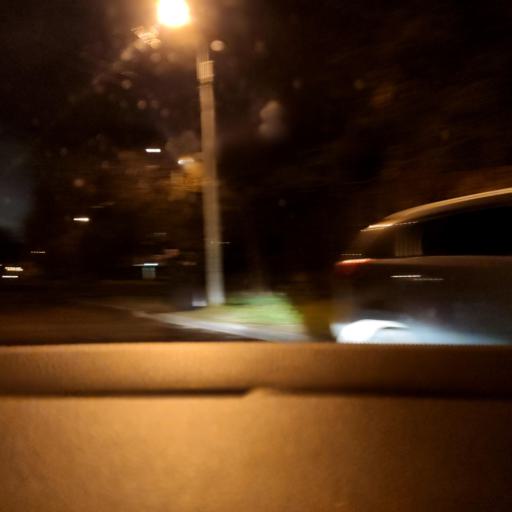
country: RU
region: Moscow
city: Vostochnyy
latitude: 55.8198
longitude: 37.8656
